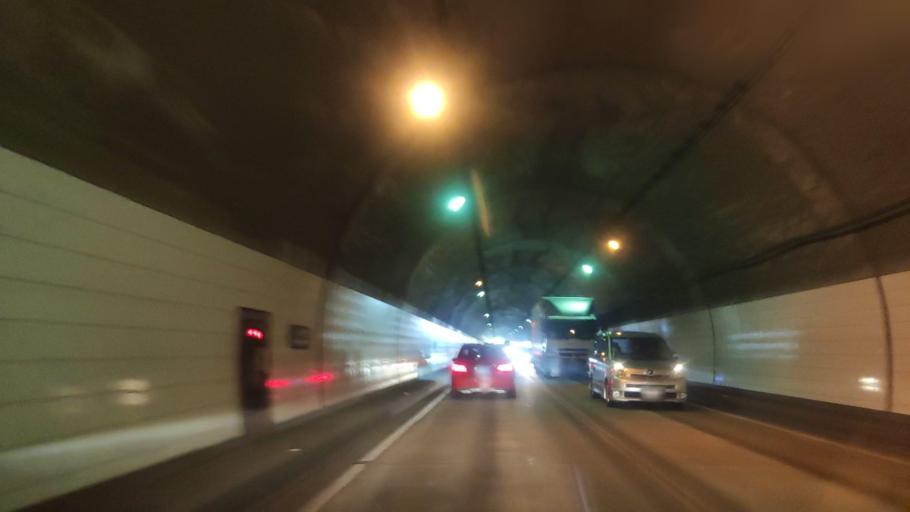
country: JP
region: Yamanashi
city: Fujikawaguchiko
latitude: 35.5330
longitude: 138.7756
